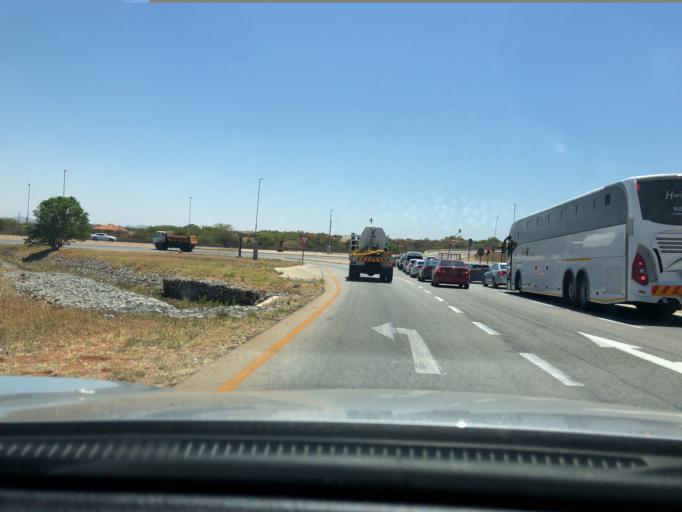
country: ZA
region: Limpopo
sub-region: Capricorn District Municipality
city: Polokwane
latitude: -23.8793
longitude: 29.5071
